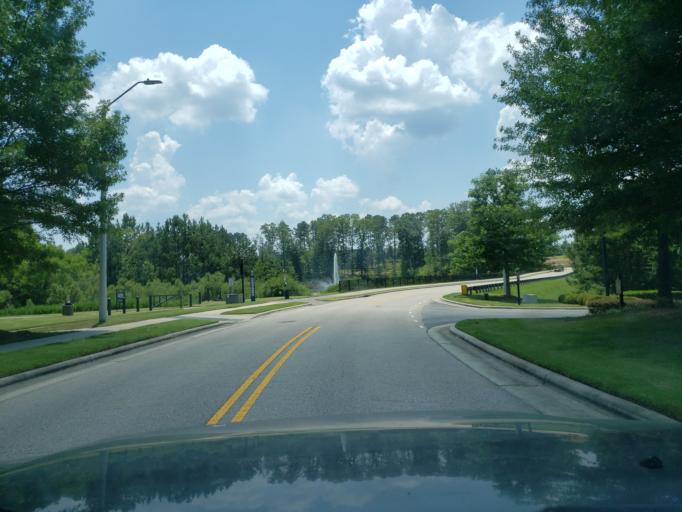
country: US
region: North Carolina
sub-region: Wake County
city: Green Level
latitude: 35.8298
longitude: -78.9146
